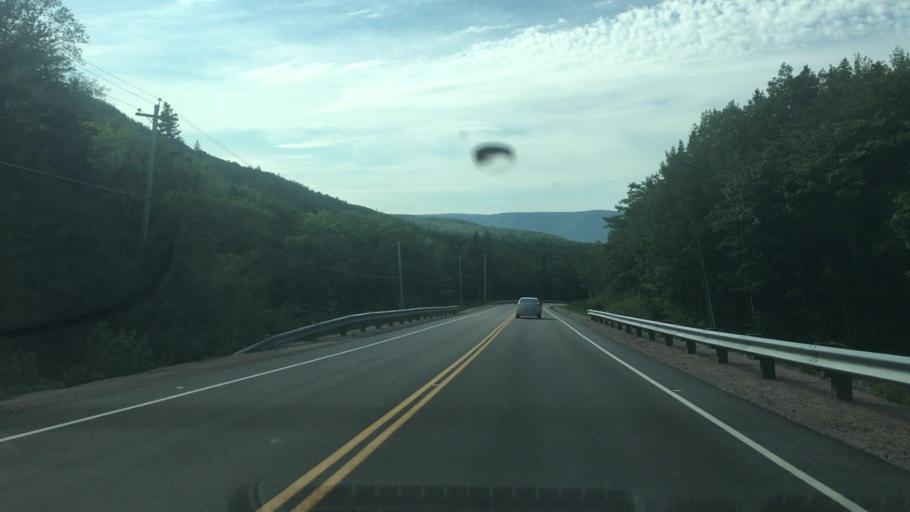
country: CA
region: Nova Scotia
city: Sydney Mines
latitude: 46.8552
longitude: -60.4550
